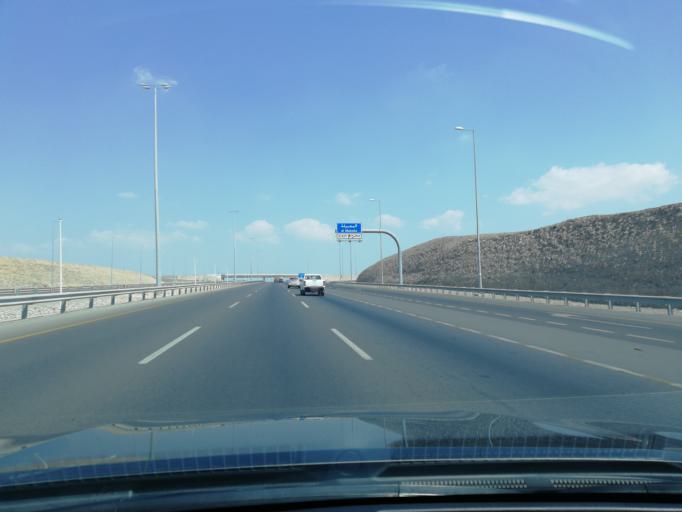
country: OM
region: Muhafazat Masqat
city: As Sib al Jadidah
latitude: 23.5907
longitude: 58.1205
